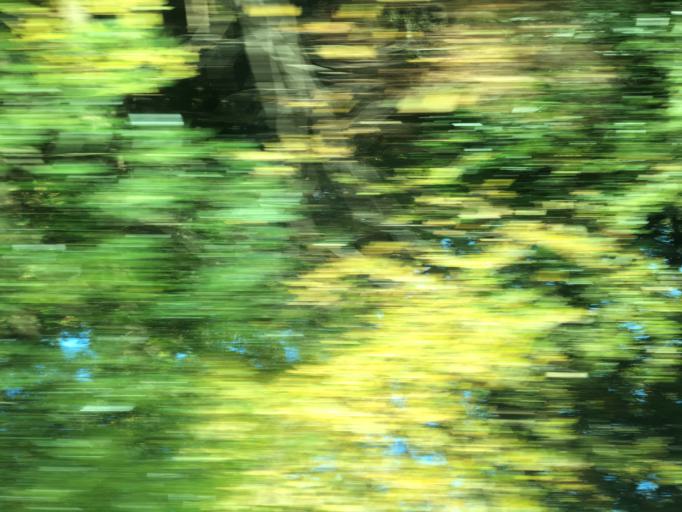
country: JP
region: Ibaraki
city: Iwase
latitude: 36.3441
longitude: 140.0704
